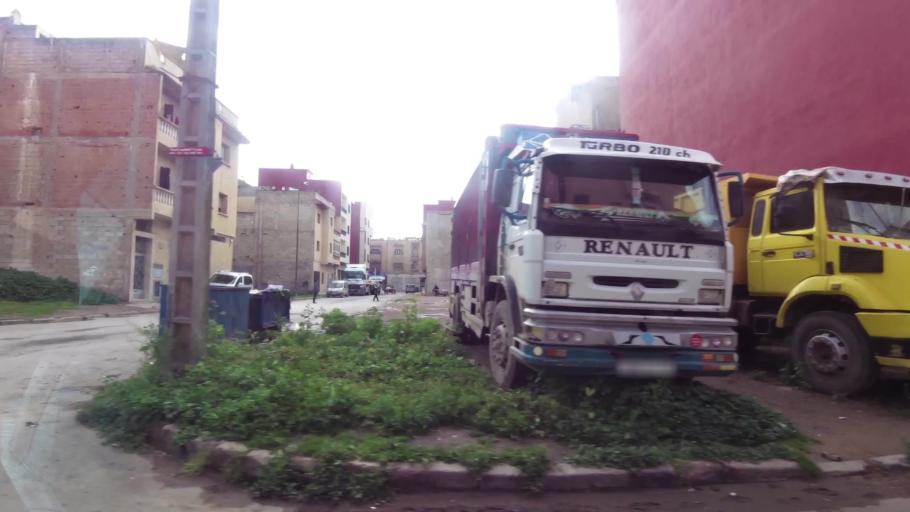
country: MA
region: Chaouia-Ouardigha
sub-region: Settat Province
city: Berrechid
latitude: 33.2672
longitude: -7.5731
